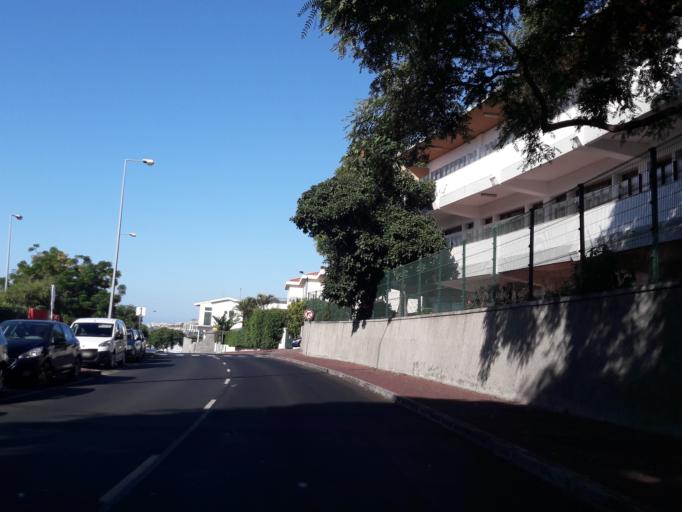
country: PT
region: Madeira
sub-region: Funchal
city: Funchal
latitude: 32.6485
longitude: -16.8920
